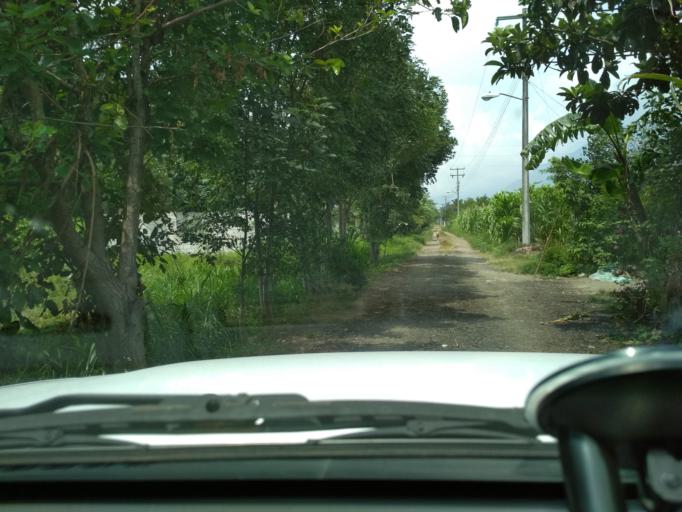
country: MX
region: Veracruz
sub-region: Nogales
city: Taza de Agua Ojo Zarco
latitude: 18.7797
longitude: -97.2165
